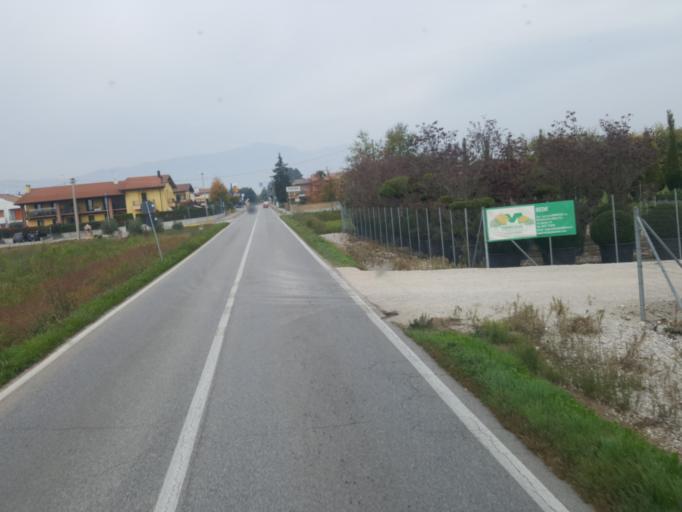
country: IT
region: Veneto
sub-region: Provincia di Treviso
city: Ramon
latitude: 45.7095
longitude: 11.8696
